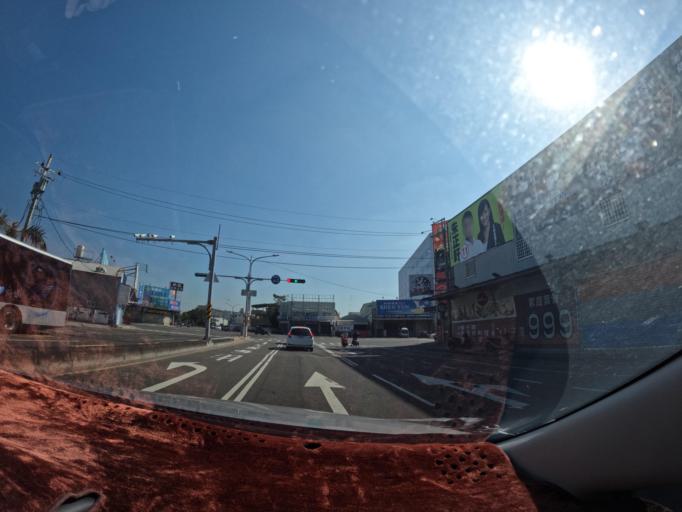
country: TW
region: Taiwan
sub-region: Tainan
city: Tainan
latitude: 22.9975
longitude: 120.2574
